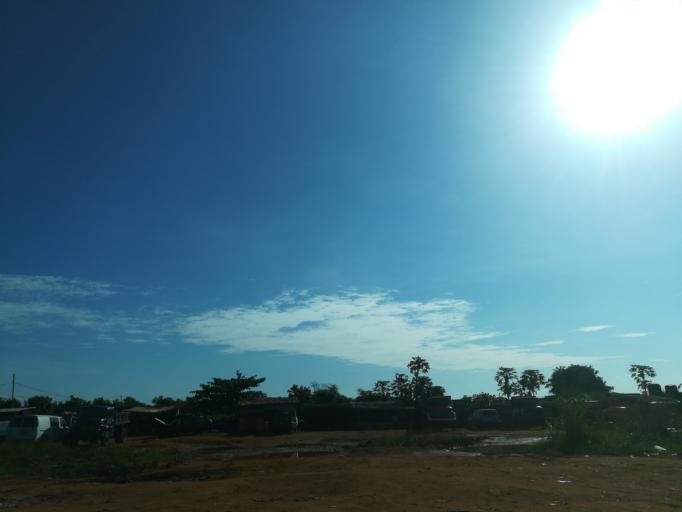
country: NG
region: Lagos
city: Ikorodu
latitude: 6.5701
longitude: 3.5323
